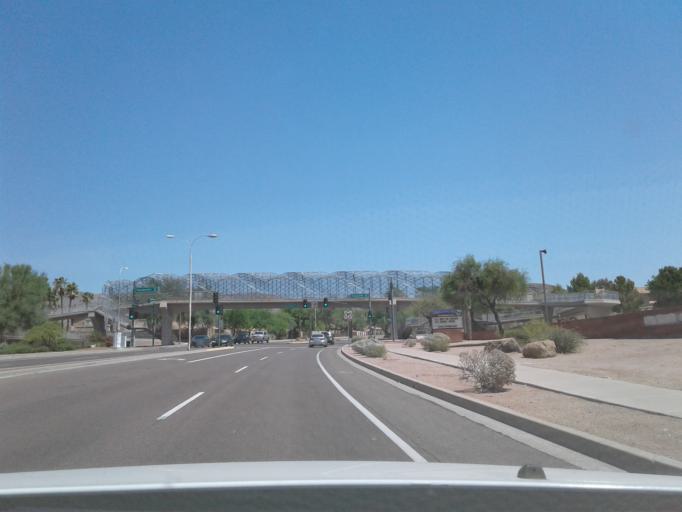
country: US
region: Arizona
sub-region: Maricopa County
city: Guadalupe
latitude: 33.3079
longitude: -112.0273
